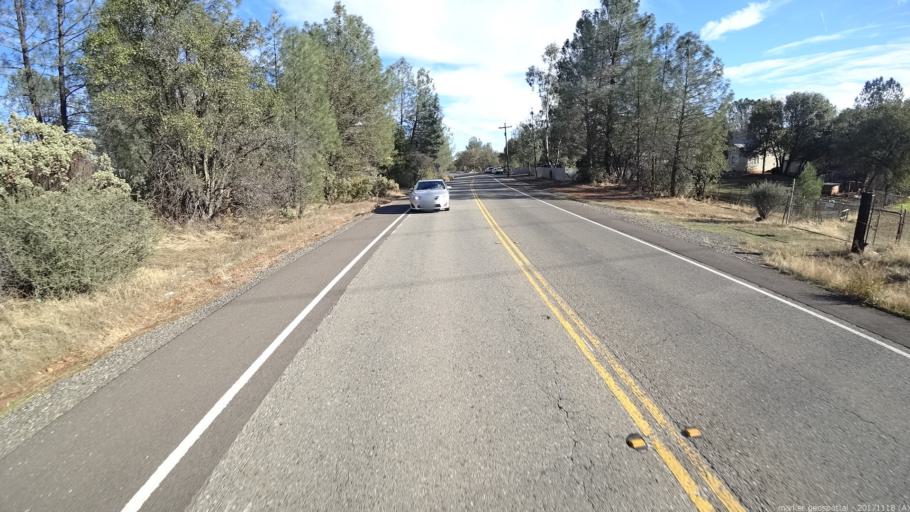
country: US
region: California
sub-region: Shasta County
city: Redding
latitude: 40.4787
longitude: -122.4264
